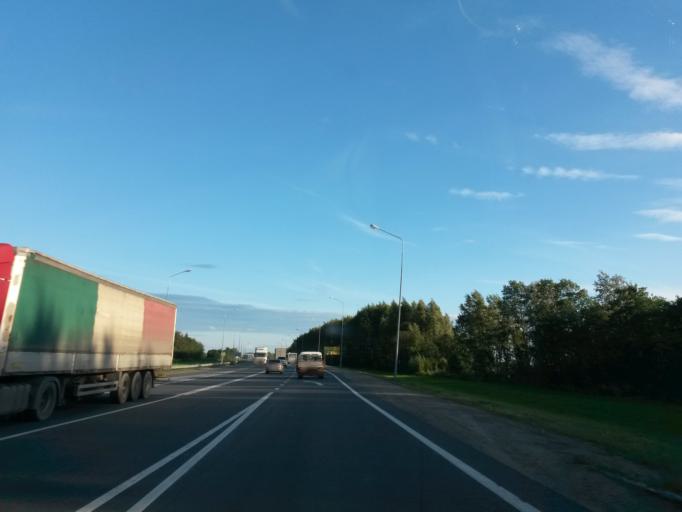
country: RU
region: Jaroslavl
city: Yaroslavl
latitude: 57.7358
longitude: 39.8962
